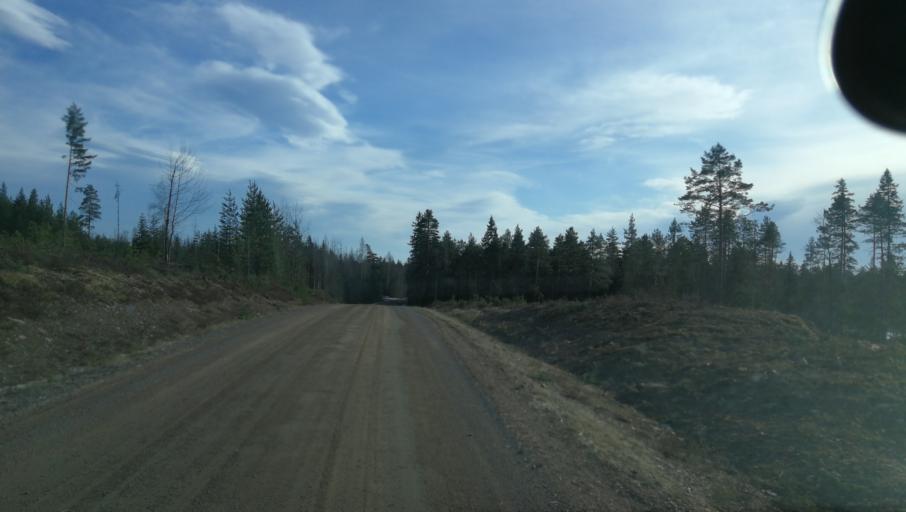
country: SE
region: Dalarna
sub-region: Vansbro Kommun
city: Vansbro
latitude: 60.8250
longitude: 14.1943
